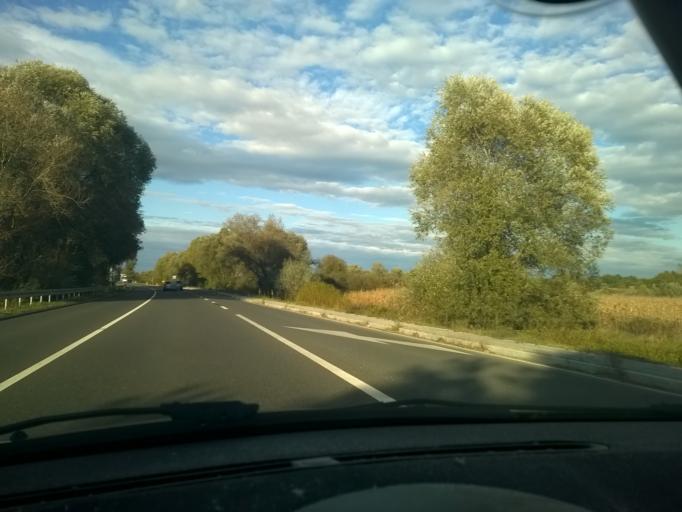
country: HR
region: Zagrebacka
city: Pojatno
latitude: 45.9128
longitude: 15.8180
